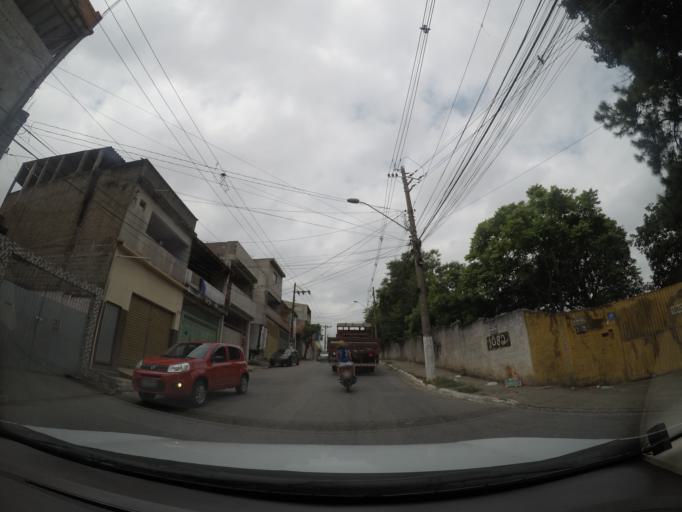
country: BR
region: Sao Paulo
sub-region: Itaquaquecetuba
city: Itaquaquecetuba
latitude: -23.4469
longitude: -46.3992
